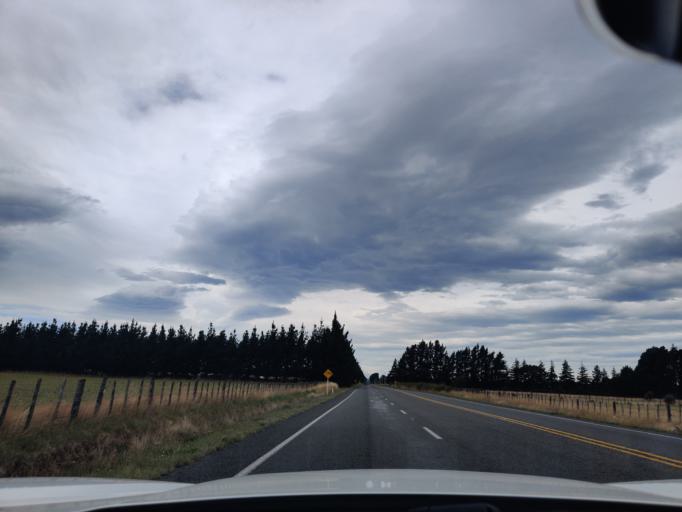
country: NZ
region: Wellington
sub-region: Masterton District
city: Masterton
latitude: -40.9927
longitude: 175.5672
